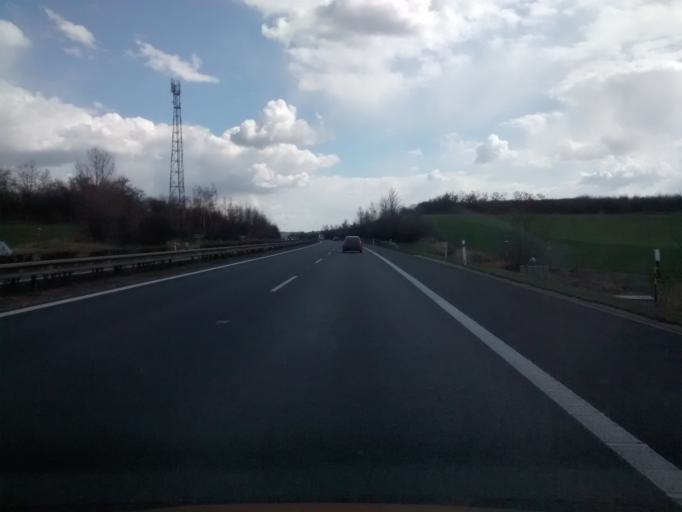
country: CZ
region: Central Bohemia
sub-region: Okres Melnik
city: Veltrusy
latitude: 50.2725
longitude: 14.3578
